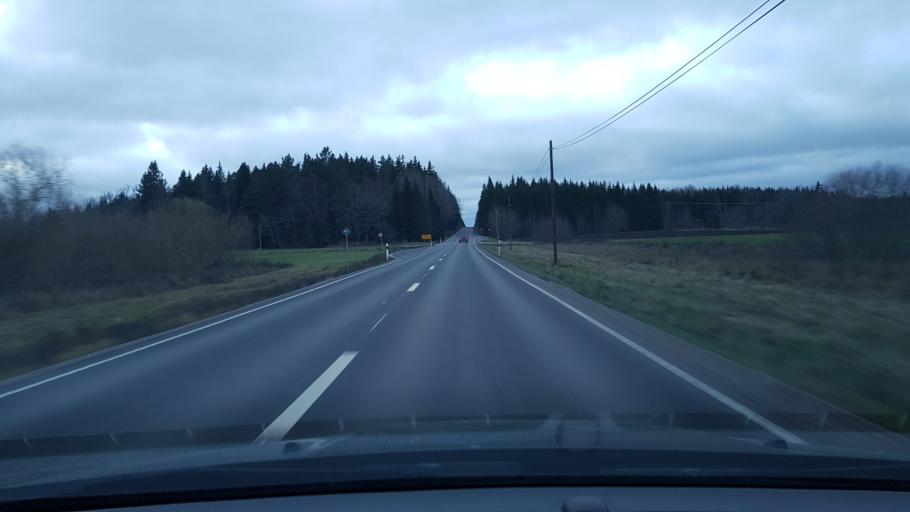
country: SE
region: Uppsala
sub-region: Uppsala Kommun
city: Vattholma
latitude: 59.9468
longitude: 17.9799
